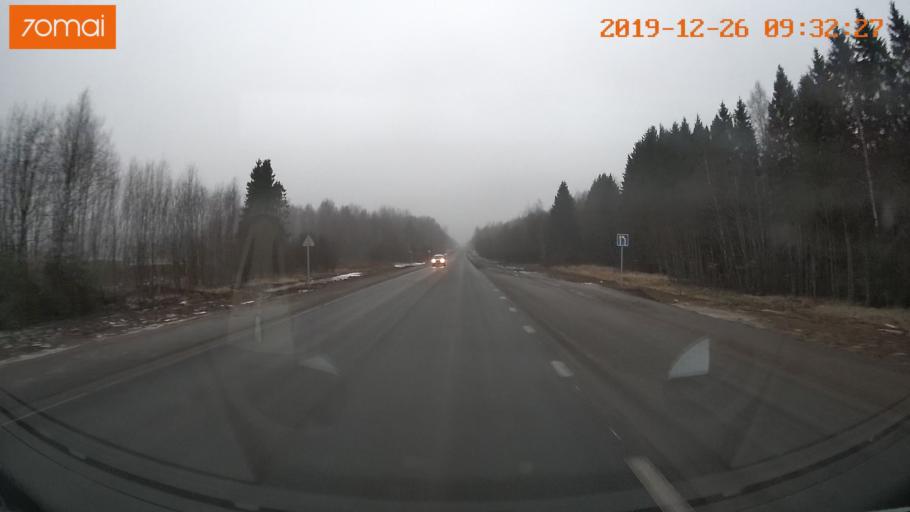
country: RU
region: Vologda
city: Gryazovets
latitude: 59.0779
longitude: 40.1164
